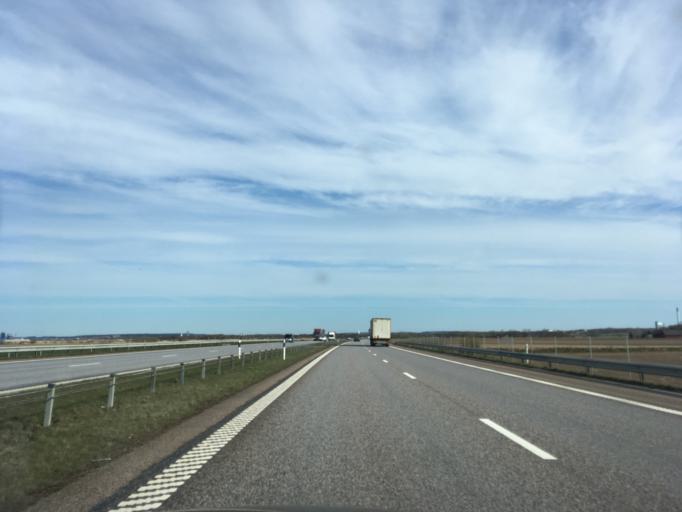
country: SE
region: Halland
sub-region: Halmstads Kommun
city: Troenninge
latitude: 56.6141
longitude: 12.9170
